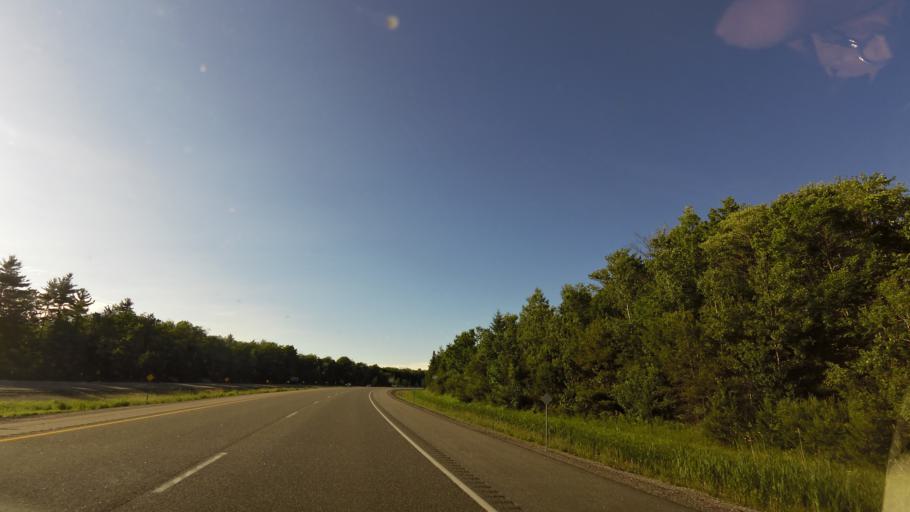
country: CA
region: Ontario
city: Barrie
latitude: 44.5425
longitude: -79.7499
